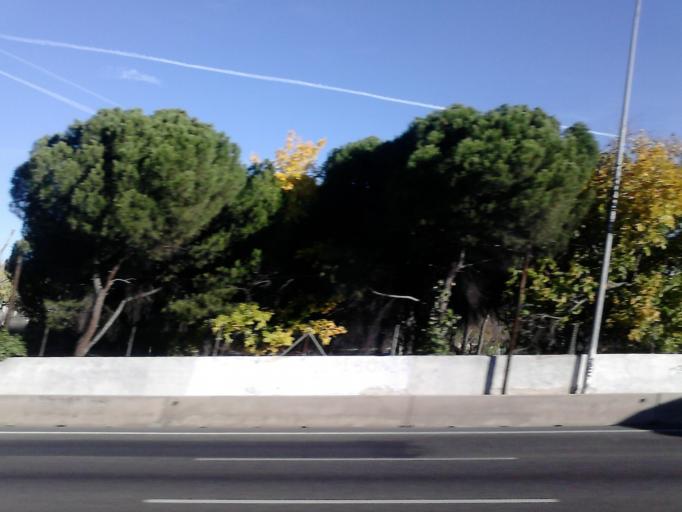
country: ES
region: Madrid
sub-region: Provincia de Madrid
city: Pozuelo de Alarcon
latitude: 40.4631
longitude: -3.7794
